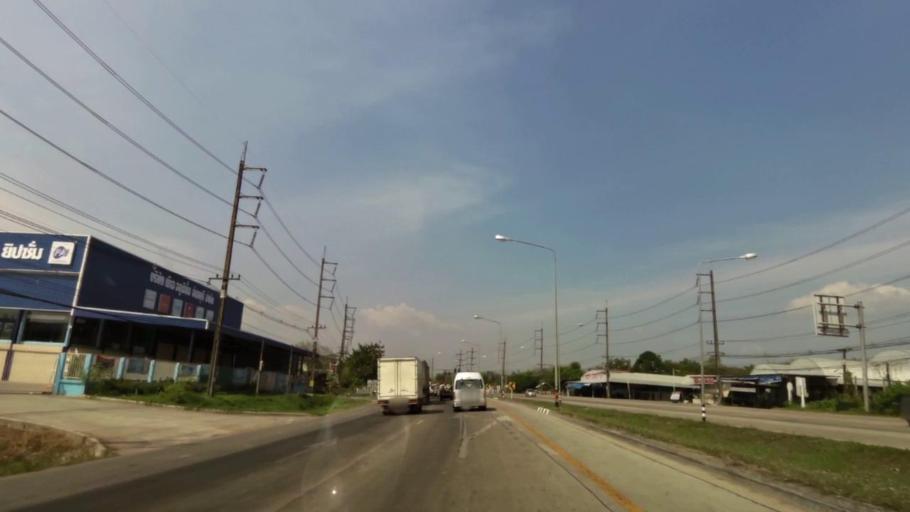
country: TH
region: Chanthaburi
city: Chanthaburi
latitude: 12.6490
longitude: 102.1294
